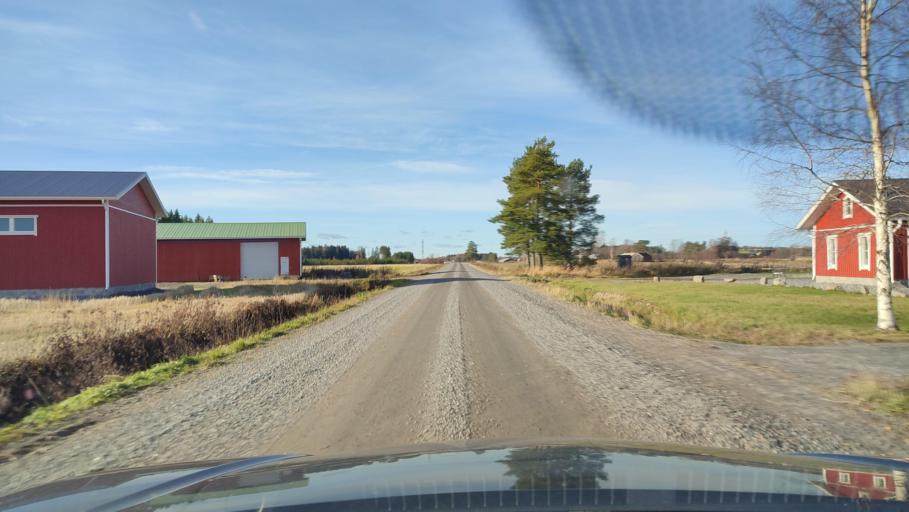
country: FI
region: Southern Ostrobothnia
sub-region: Suupohja
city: Teuva
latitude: 62.4579
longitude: 21.6631
